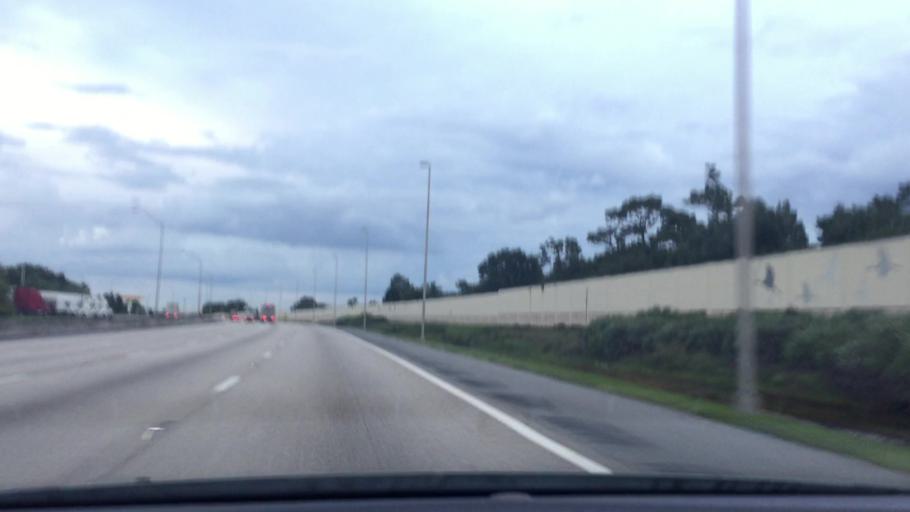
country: US
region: Florida
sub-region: Orange County
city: Gotha
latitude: 28.5147
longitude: -81.5012
